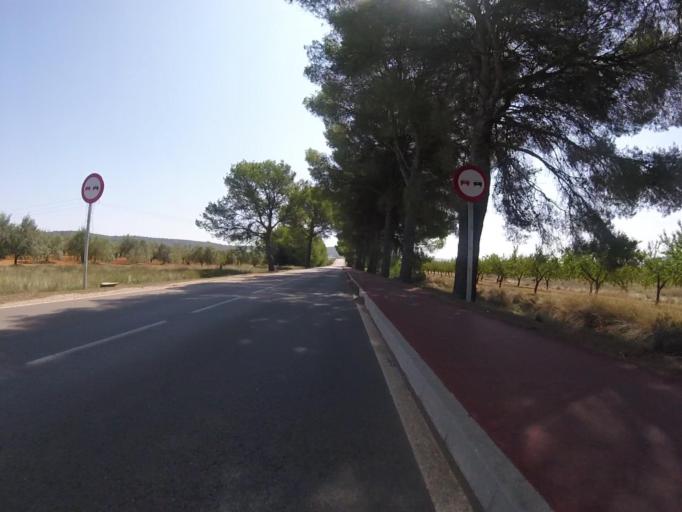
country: ES
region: Valencia
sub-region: Provincia de Castello
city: Cabanes
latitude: 40.1596
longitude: 0.0315
